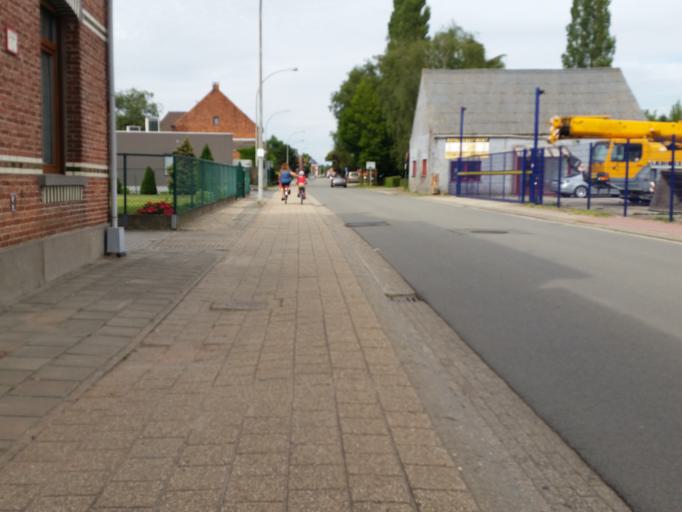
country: BE
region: Flanders
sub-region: Provincie Antwerpen
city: Willebroek
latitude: 51.0418
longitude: 4.3321
